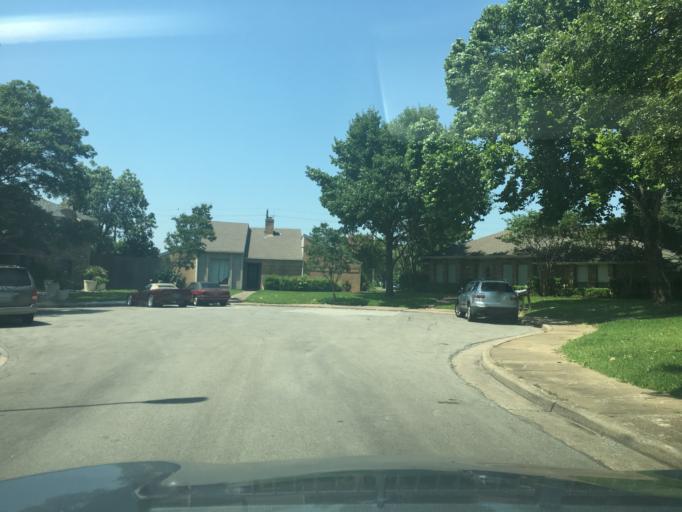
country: US
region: Texas
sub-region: Dallas County
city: Richardson
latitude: 32.9305
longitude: -96.7101
